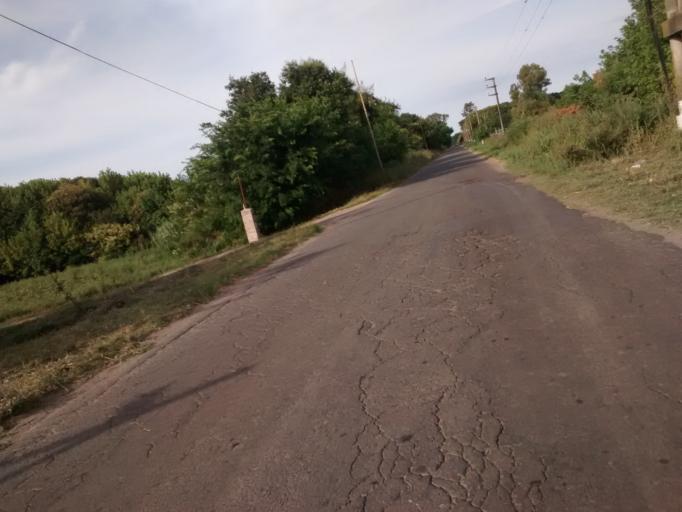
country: AR
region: Buenos Aires
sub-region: Partido de La Plata
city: La Plata
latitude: -34.8454
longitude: -58.0964
